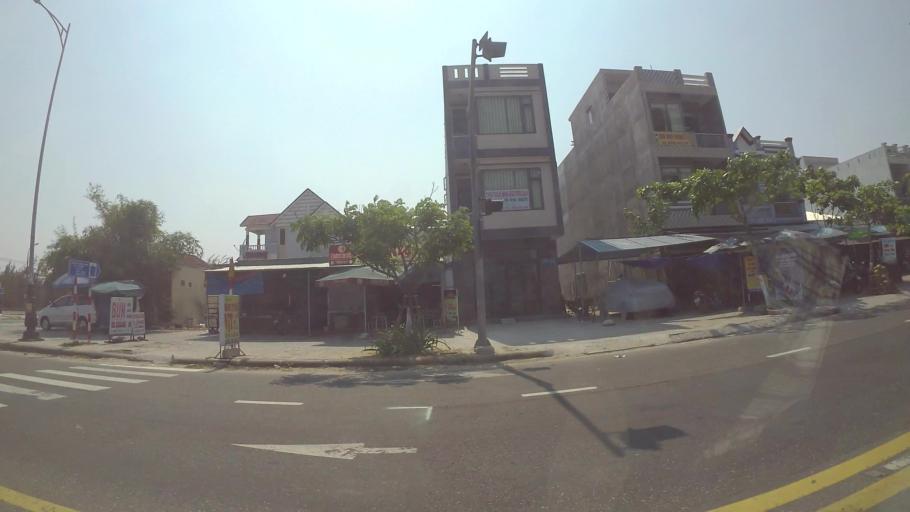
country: VN
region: Da Nang
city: Ngu Hanh Son
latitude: 15.9813
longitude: 108.2757
